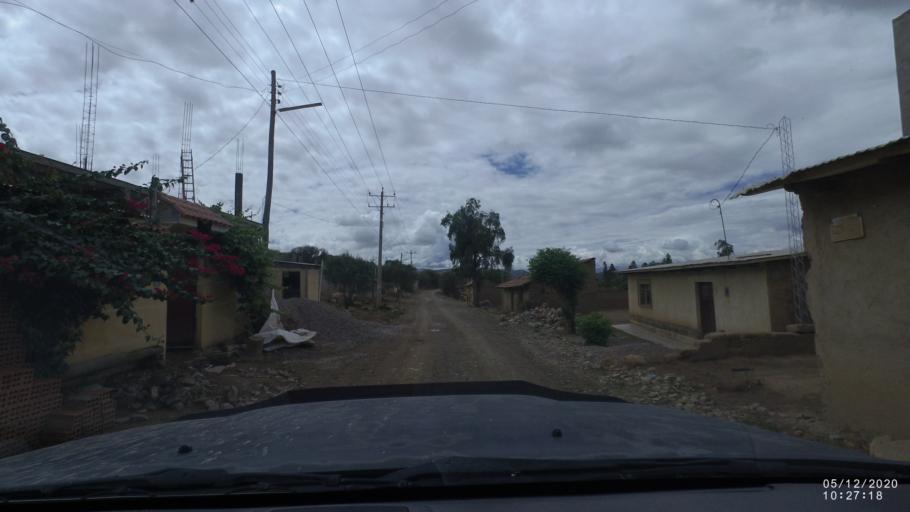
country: BO
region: Cochabamba
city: Sipe Sipe
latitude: -17.5319
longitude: -66.2791
